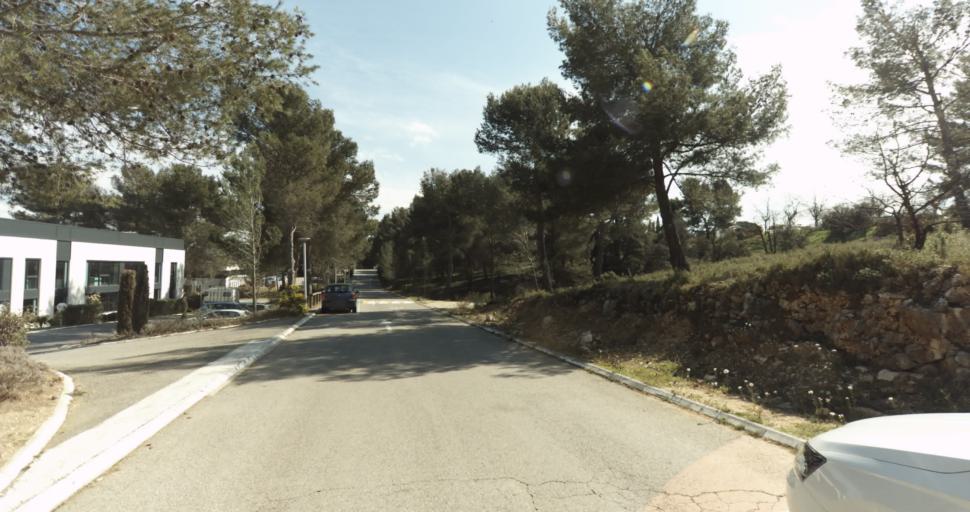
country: FR
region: Provence-Alpes-Cote d'Azur
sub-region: Departement des Bouches-du-Rhone
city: Cabries
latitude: 43.4822
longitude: 5.3617
